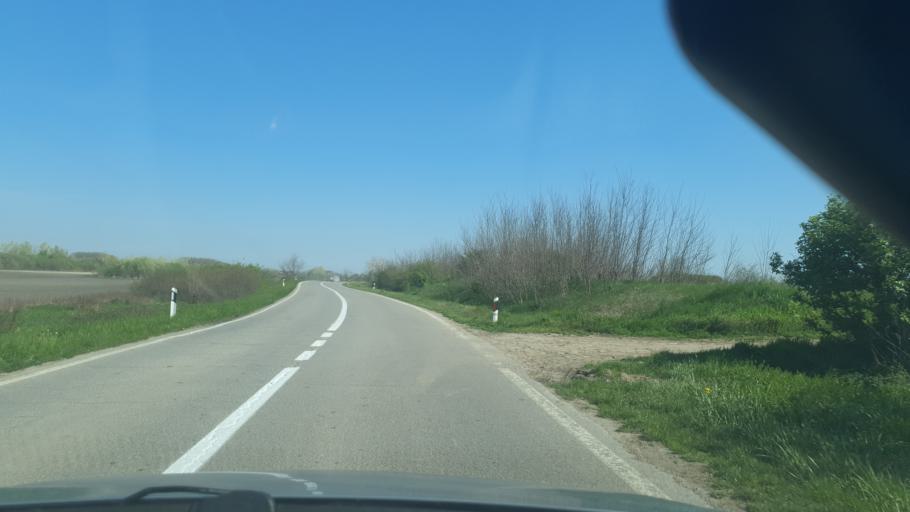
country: RS
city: Kolut
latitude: 45.8675
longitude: 18.9342
